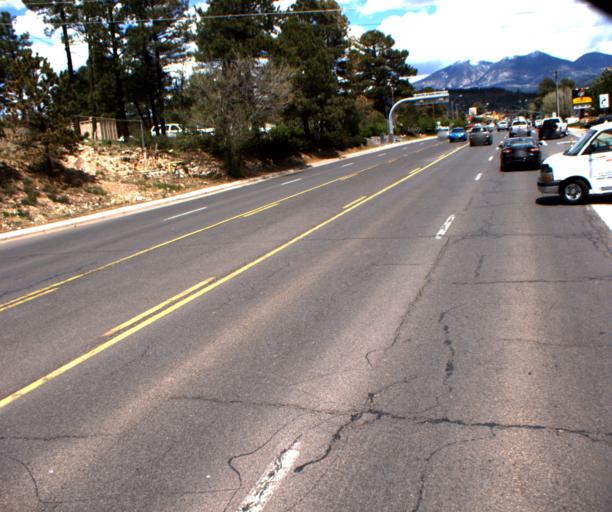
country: US
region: Arizona
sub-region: Coconino County
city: Flagstaff
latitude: 35.1807
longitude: -111.6612
